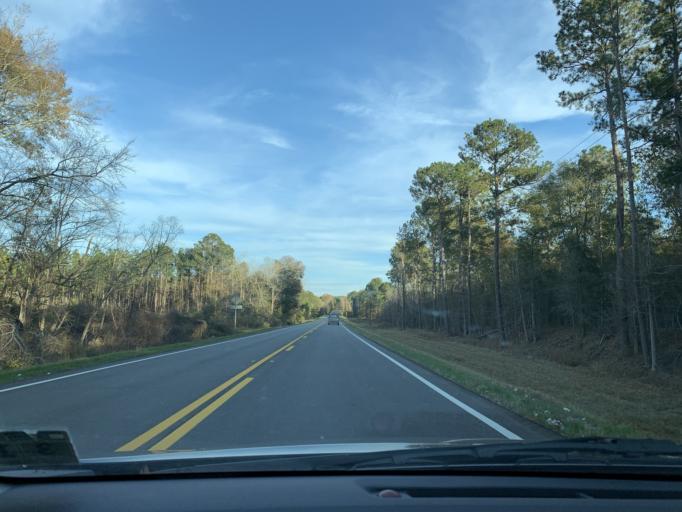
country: US
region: Georgia
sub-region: Irwin County
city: Ocilla
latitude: 31.5954
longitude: -83.1194
